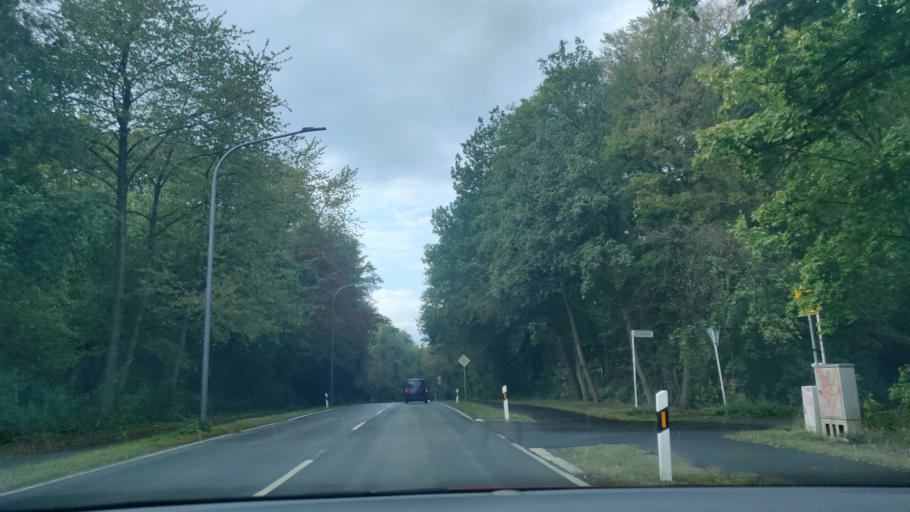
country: DE
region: North Rhine-Westphalia
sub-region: Regierungsbezirk Dusseldorf
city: Wuppertal
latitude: 51.2835
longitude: 7.1150
